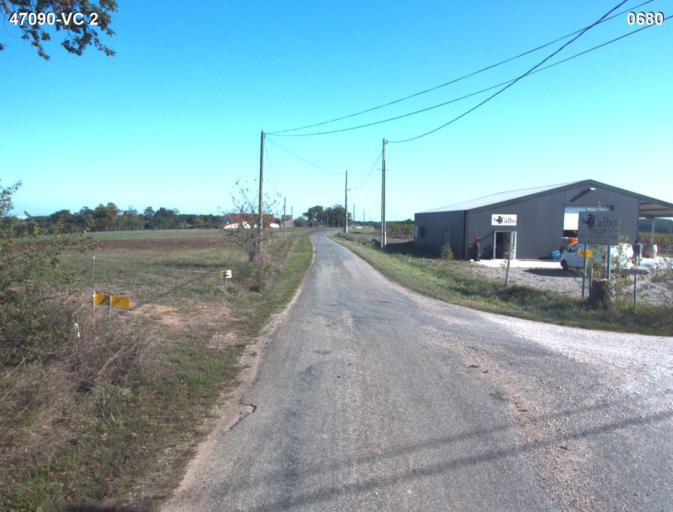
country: FR
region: Aquitaine
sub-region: Departement du Lot-et-Garonne
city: Vianne
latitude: 44.1853
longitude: 0.3655
